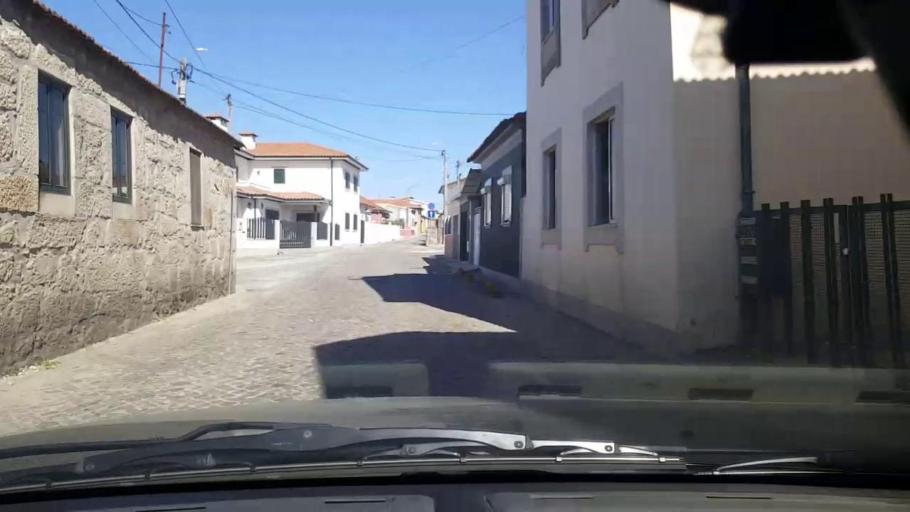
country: PT
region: Porto
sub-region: Maia
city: Gemunde
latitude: 41.2862
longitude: -8.6737
